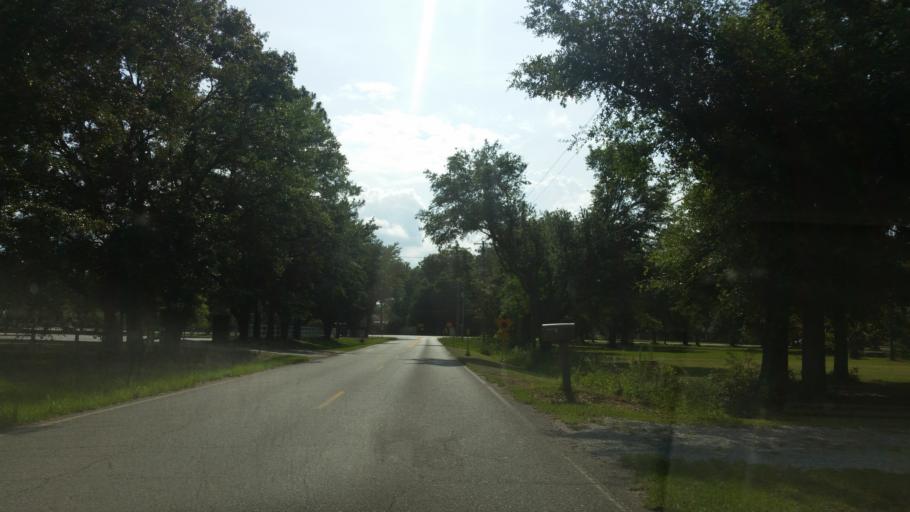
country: US
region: Florida
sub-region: Escambia County
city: Ensley
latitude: 30.5414
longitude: -87.3112
